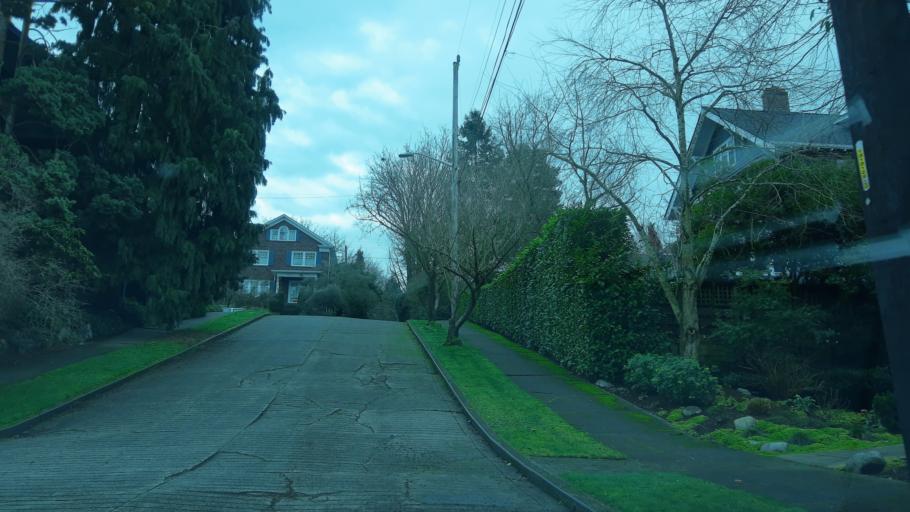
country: US
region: Washington
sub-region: King County
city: Seattle
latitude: 47.6378
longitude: -122.3173
